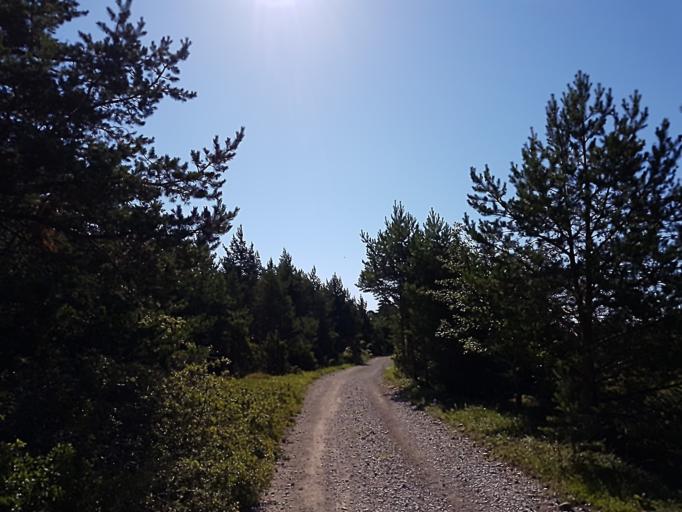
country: SE
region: Gotland
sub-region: Gotland
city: Visby
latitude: 57.6114
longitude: 18.3627
